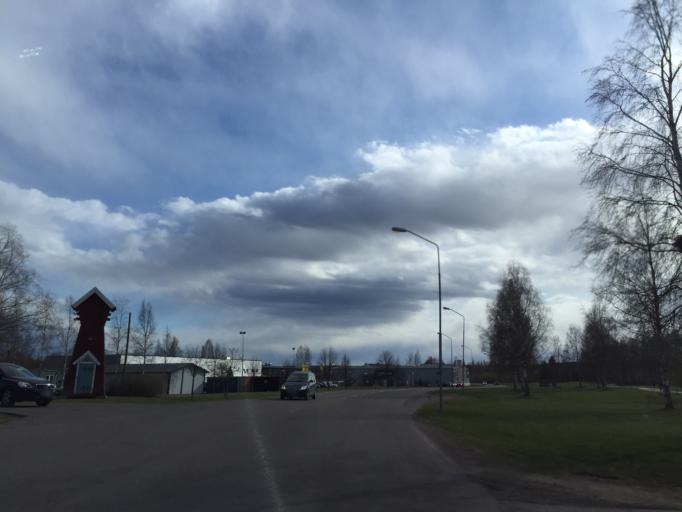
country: SE
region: Dalarna
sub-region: Borlange Kommun
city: Borlaenge
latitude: 60.4798
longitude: 15.4087
